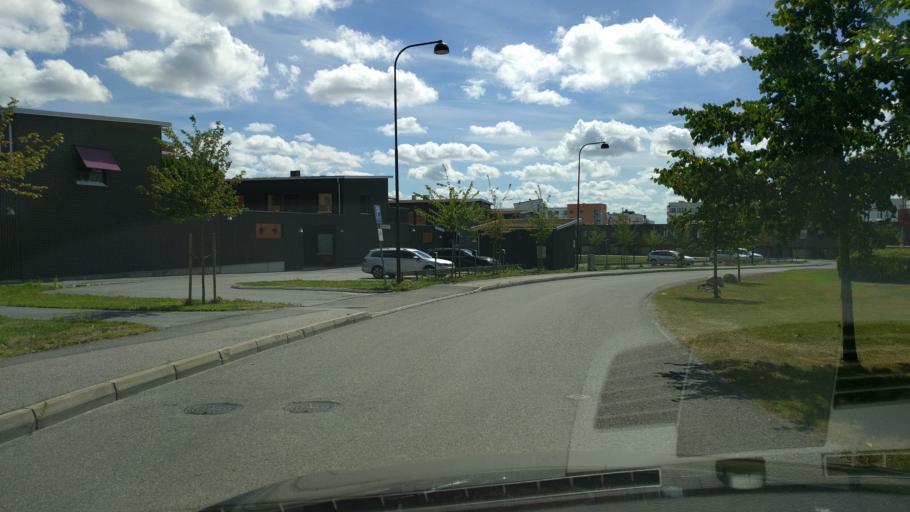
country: SE
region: Stockholm
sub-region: Jarfalla Kommun
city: Jakobsberg
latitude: 59.4180
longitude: 17.8641
